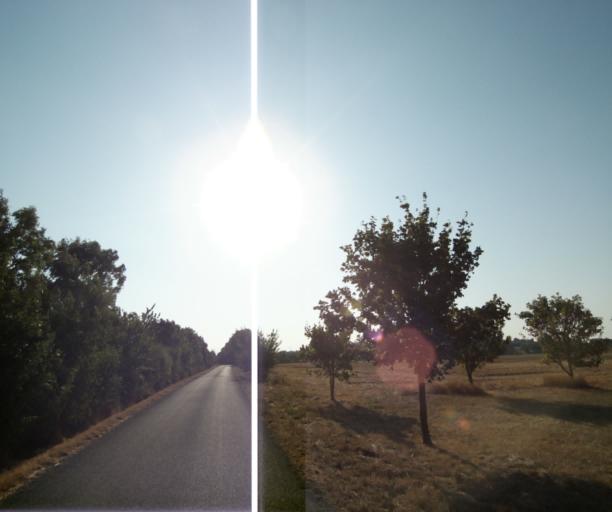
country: FR
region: Poitou-Charentes
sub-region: Departement de la Charente-Maritime
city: Muron
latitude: 45.9828
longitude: -0.8159
